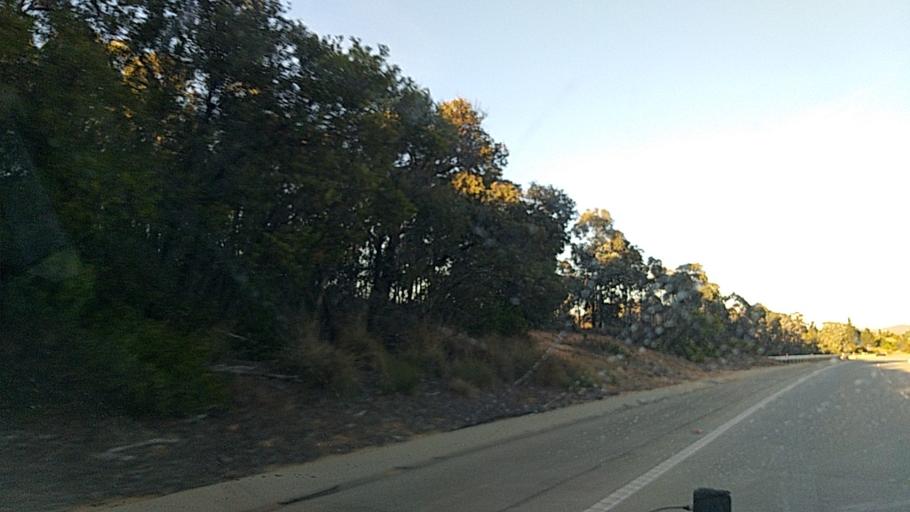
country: AU
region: New South Wales
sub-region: Yass Valley
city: Gundaroo
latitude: -35.1116
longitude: 149.3661
